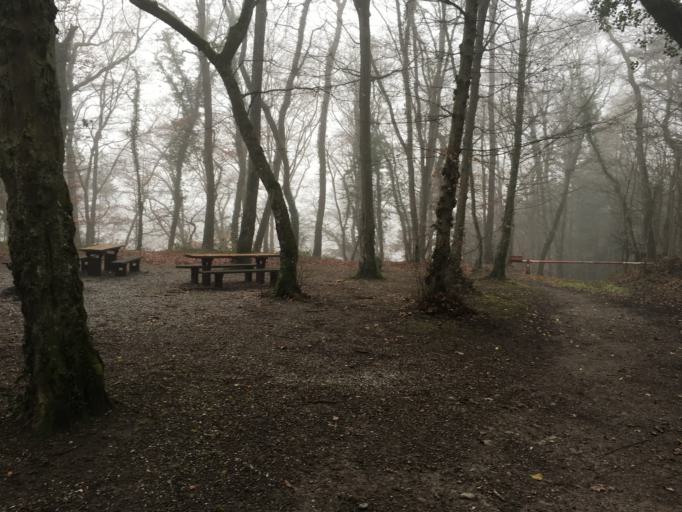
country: CH
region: Aargau
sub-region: Bezirk Zurzach
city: Koblenz
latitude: 47.6142
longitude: 8.2627
